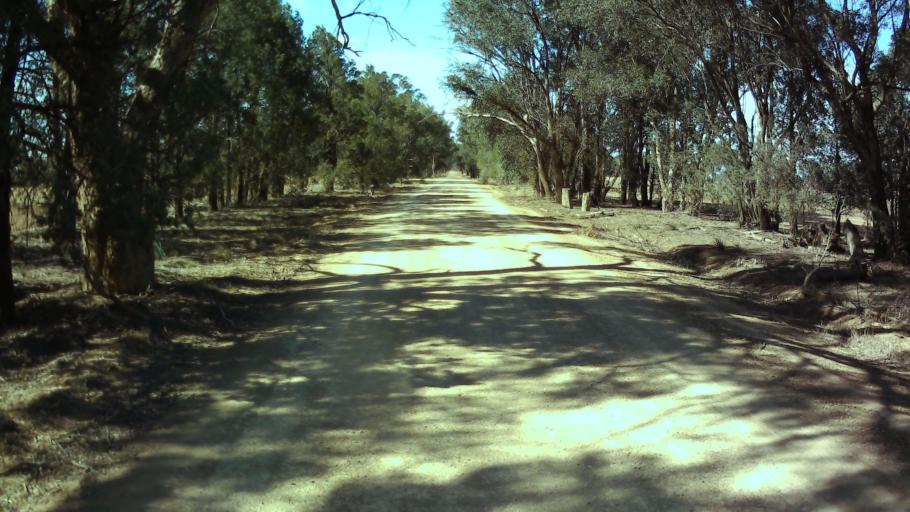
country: AU
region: New South Wales
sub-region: Weddin
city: Grenfell
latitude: -34.0409
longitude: 148.3157
